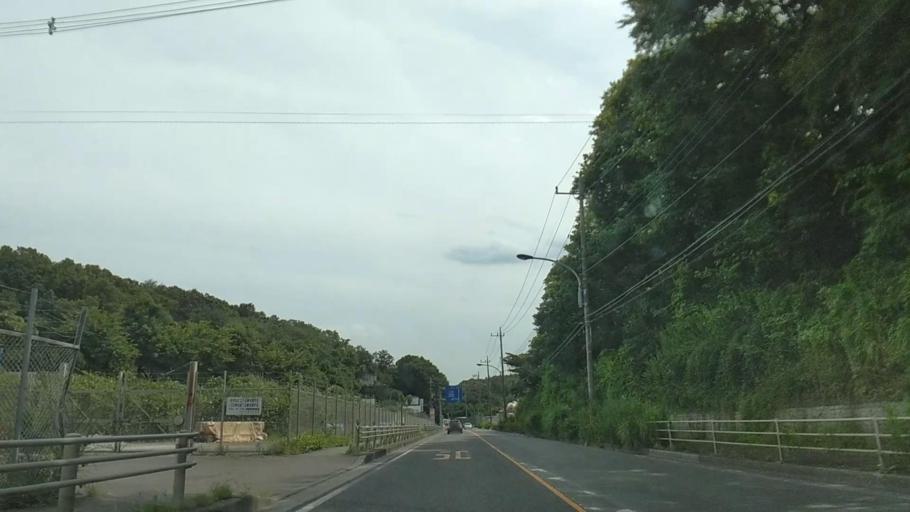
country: JP
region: Tokyo
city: Hachioji
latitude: 35.6197
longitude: 139.3410
